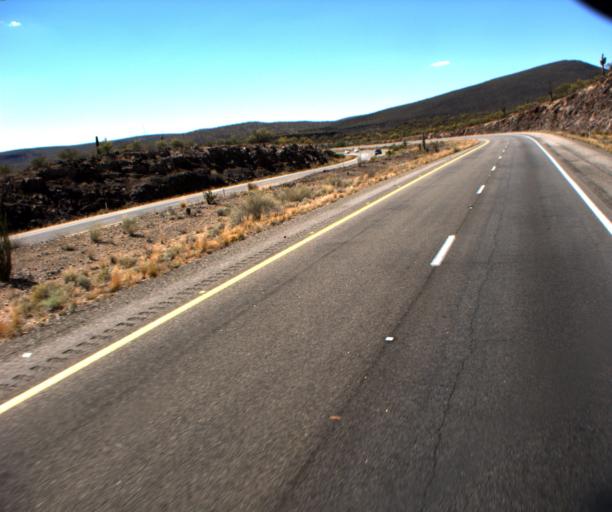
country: US
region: Arizona
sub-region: Yavapai County
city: Bagdad
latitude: 34.5418
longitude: -113.4367
